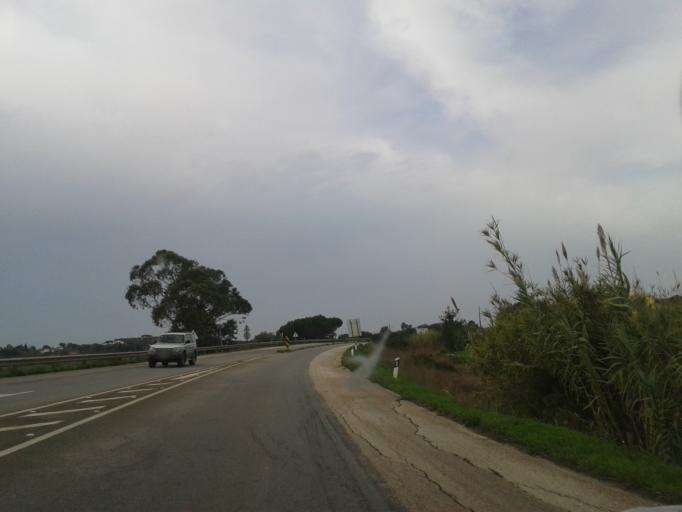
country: PT
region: Faro
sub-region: Lagos
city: Lagos
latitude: 37.0983
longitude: -8.7388
